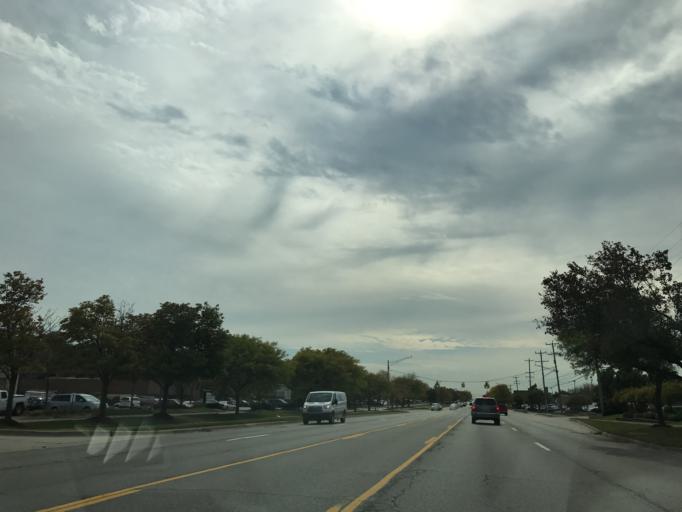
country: US
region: Michigan
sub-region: Oakland County
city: Farmington Hills
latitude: 42.5087
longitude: -83.3592
